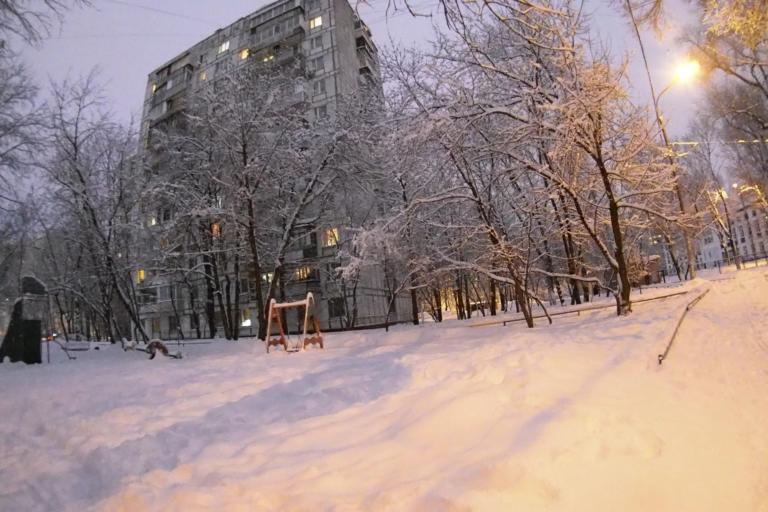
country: RU
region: Moscow
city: Perovo
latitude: 55.7469
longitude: 37.7906
